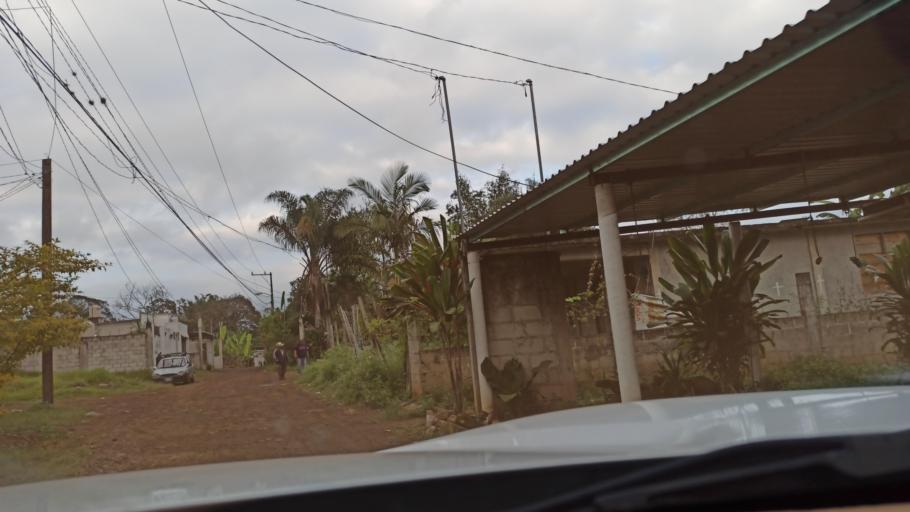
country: MX
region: Veracruz
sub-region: Fortin
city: Monte Salas
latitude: 18.9273
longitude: -97.0113
